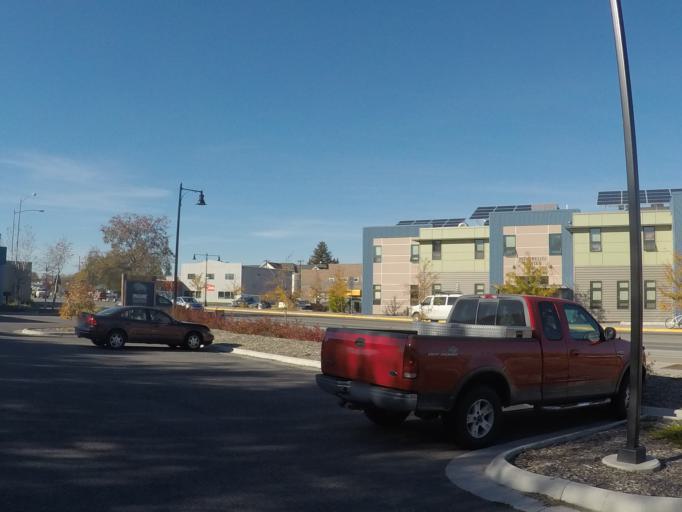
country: US
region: Montana
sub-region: Missoula County
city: Missoula
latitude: 46.8764
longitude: -114.0090
